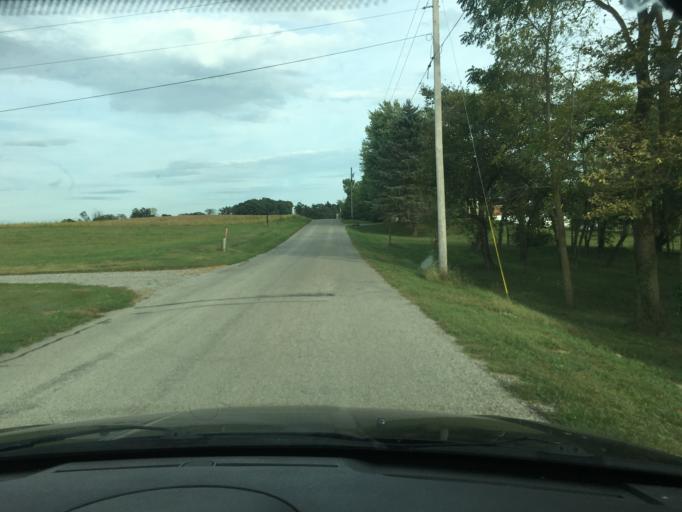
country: US
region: Ohio
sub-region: Logan County
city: Bellefontaine
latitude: 40.3131
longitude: -83.7433
